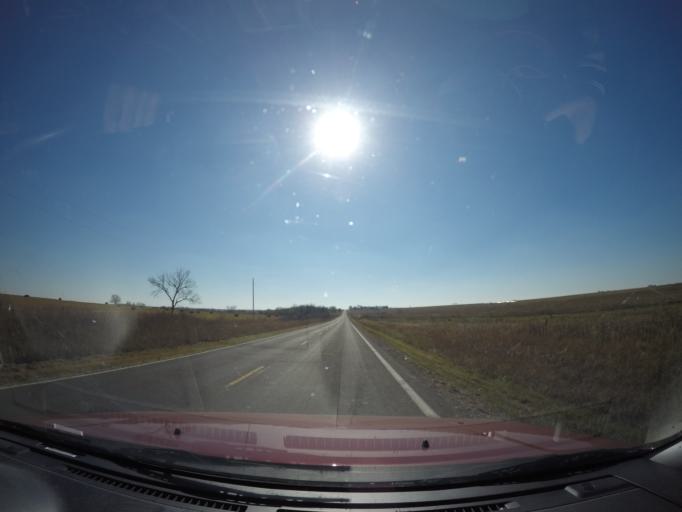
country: US
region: Kansas
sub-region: Morris County
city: Council Grove
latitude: 38.7789
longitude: -96.5013
